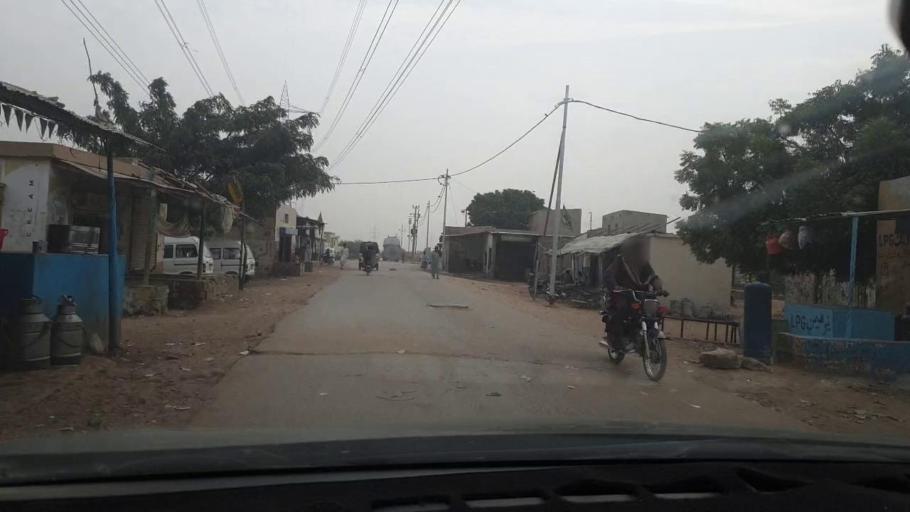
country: PK
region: Sindh
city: Malir Cantonment
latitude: 24.9067
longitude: 67.2861
